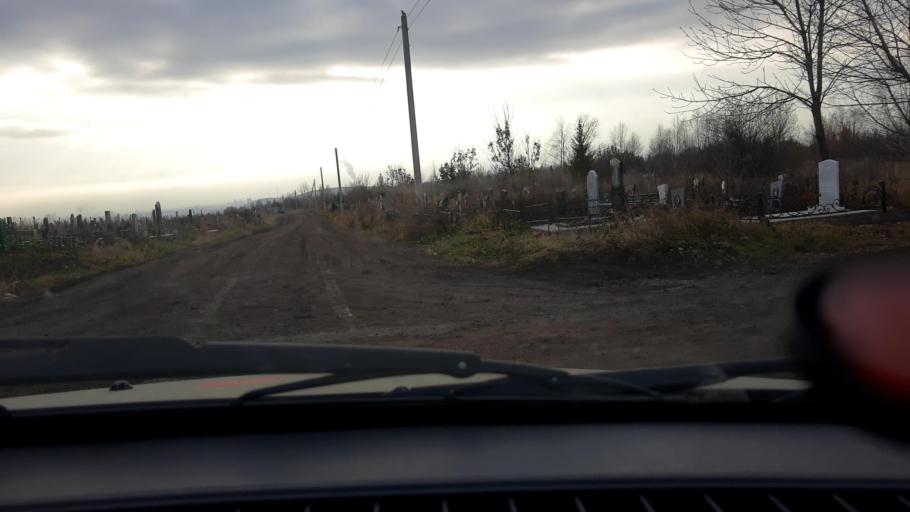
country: RU
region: Bashkortostan
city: Ufa
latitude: 54.8575
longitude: 56.1649
